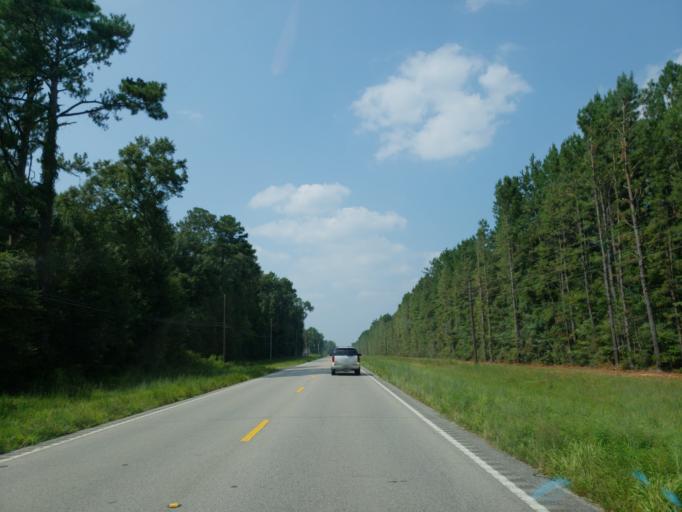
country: US
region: Mississippi
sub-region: Forrest County
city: Glendale
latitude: 31.4242
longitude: -89.2809
